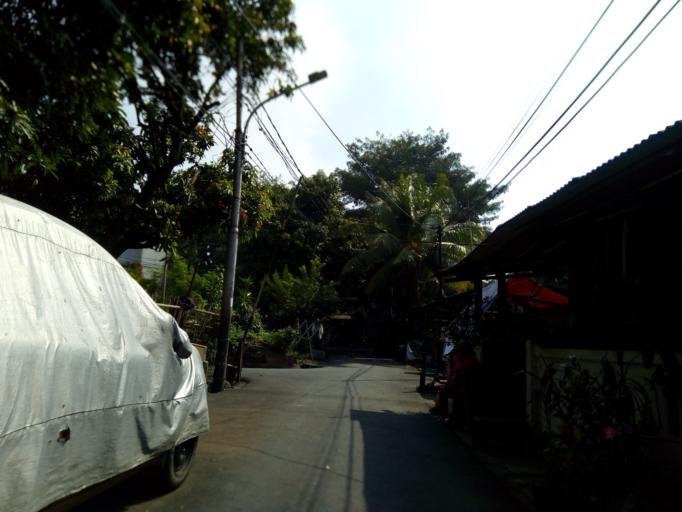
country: ID
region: Jakarta Raya
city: Jakarta
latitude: -6.2061
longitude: 106.8327
